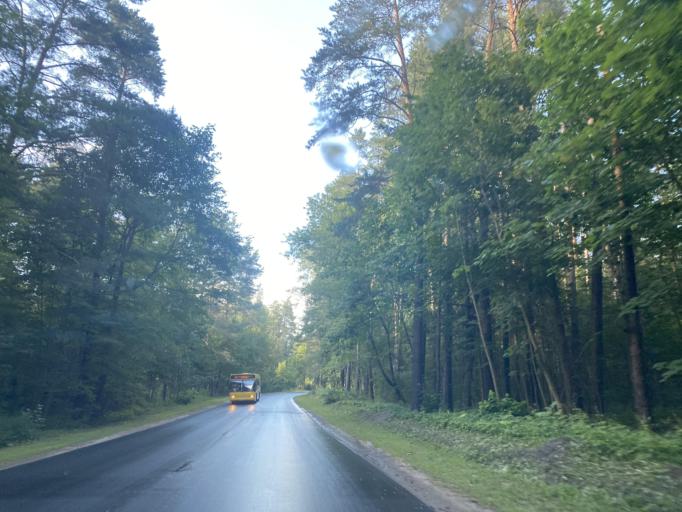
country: BY
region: Minsk
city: Borovlyany
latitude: 53.9219
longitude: 27.6538
